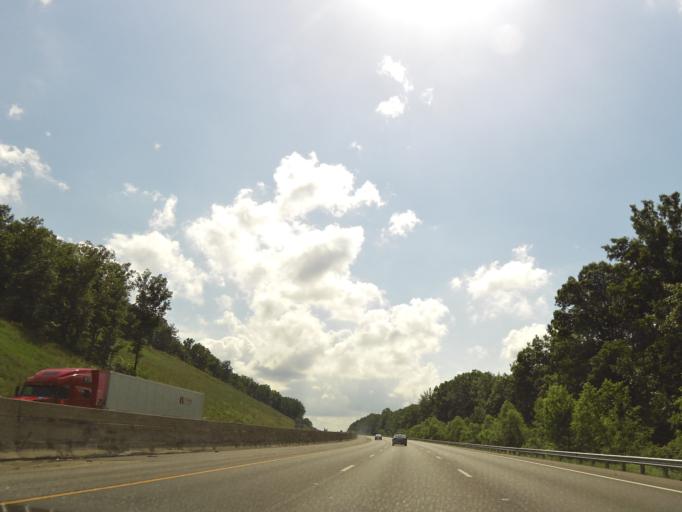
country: US
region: Alabama
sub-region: Saint Clair County
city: Pell City
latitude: 33.5994
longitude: -86.3356
